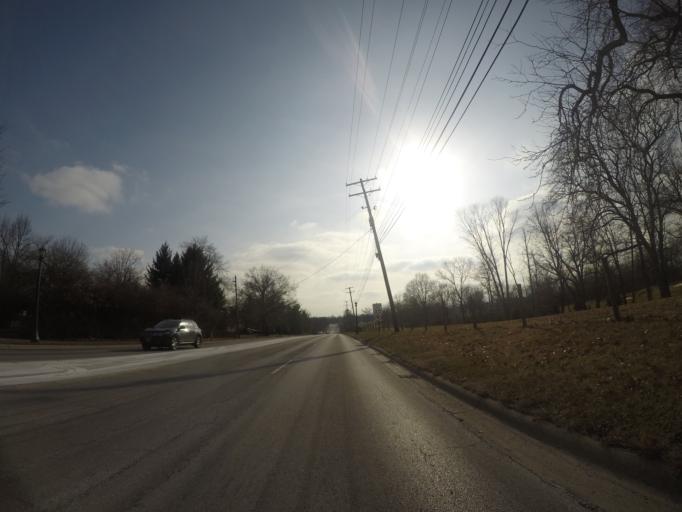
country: US
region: Ohio
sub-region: Franklin County
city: Upper Arlington
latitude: 40.0383
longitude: -83.0507
